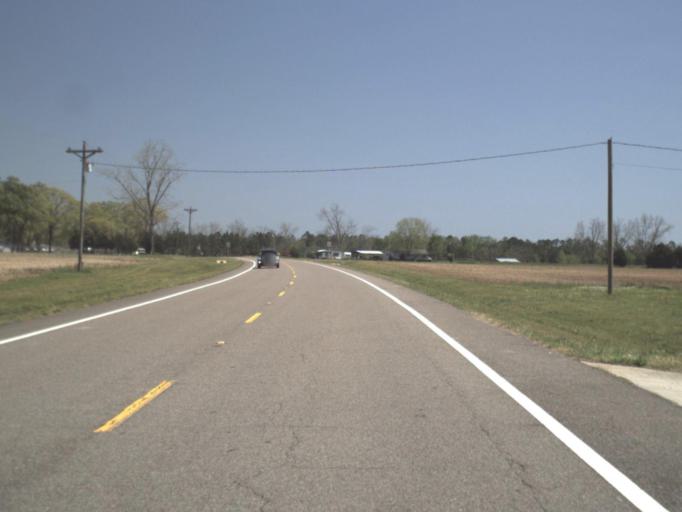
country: US
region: Alabama
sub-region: Escambia County
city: East Brewton
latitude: 30.9017
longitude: -87.0298
